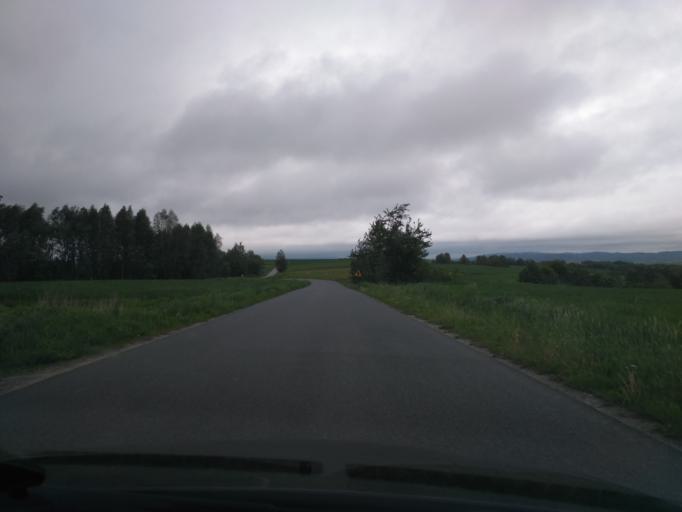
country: PL
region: Subcarpathian Voivodeship
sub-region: Powiat debicki
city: Jodlowa
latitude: 49.8686
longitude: 21.3140
